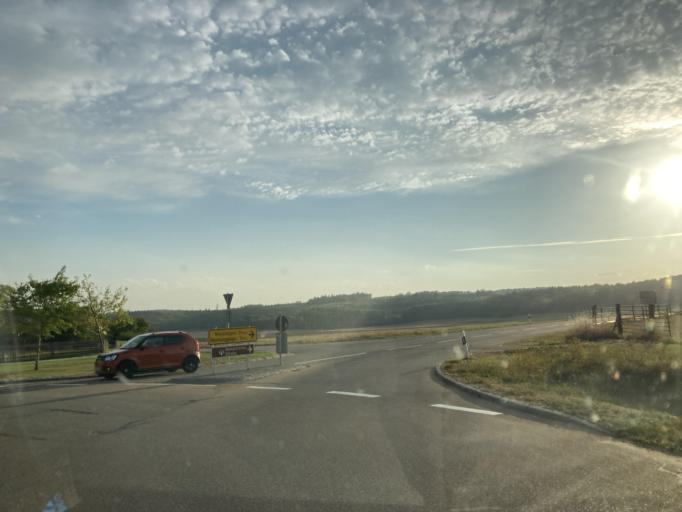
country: DE
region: Bavaria
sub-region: Swabia
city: Bissingen
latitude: 48.7630
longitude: 10.6372
